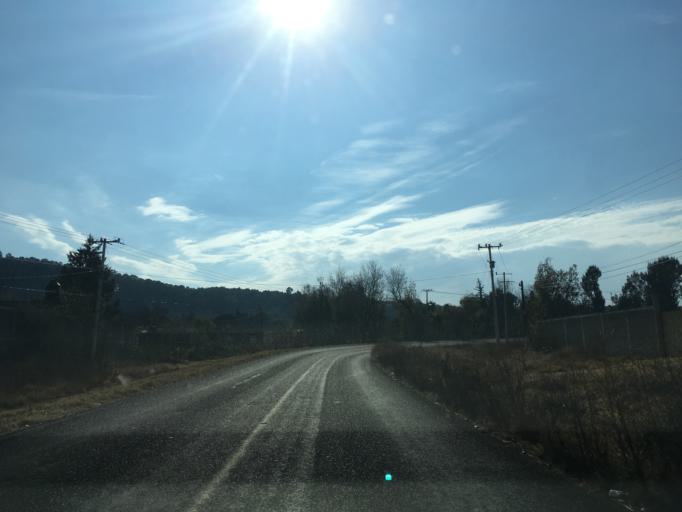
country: MX
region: Michoacan
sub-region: Patzcuaro
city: Santa Ana Chapitiro
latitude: 19.5286
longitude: -101.6466
